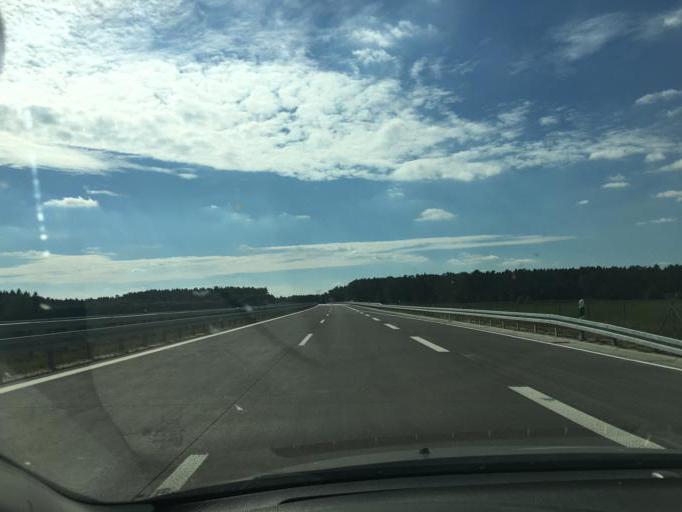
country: DE
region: Mecklenburg-Vorpommern
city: Gross Laasch
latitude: 53.3799
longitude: 11.5231
